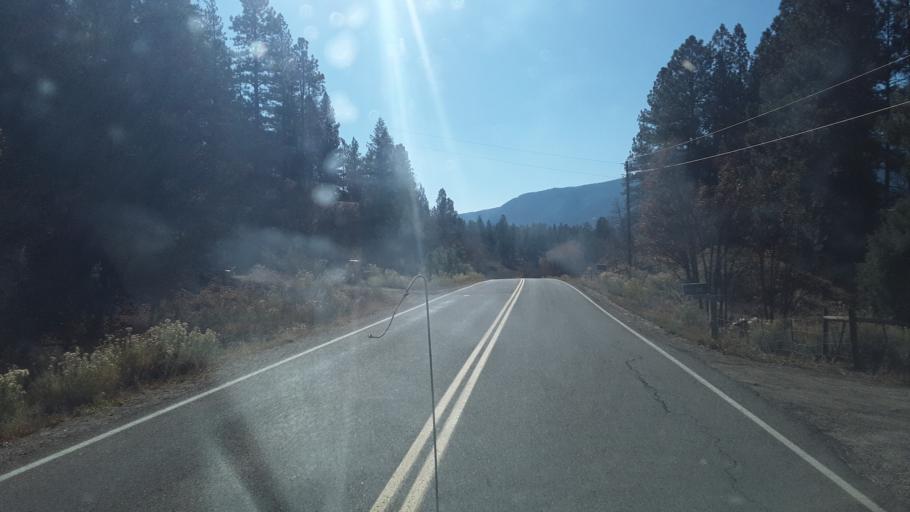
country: US
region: Colorado
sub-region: La Plata County
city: Durango
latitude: 37.4164
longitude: -107.8044
